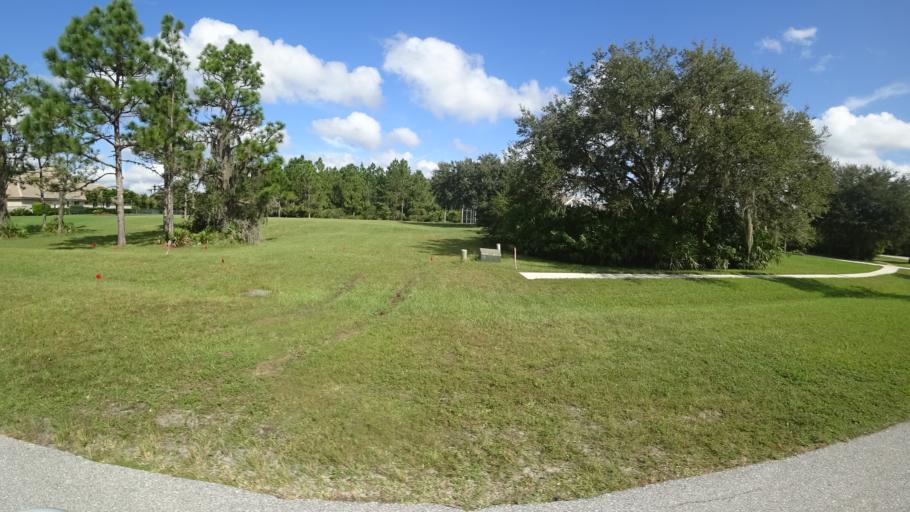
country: US
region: Florida
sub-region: Sarasota County
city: Fruitville
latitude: 27.3949
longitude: -82.3131
